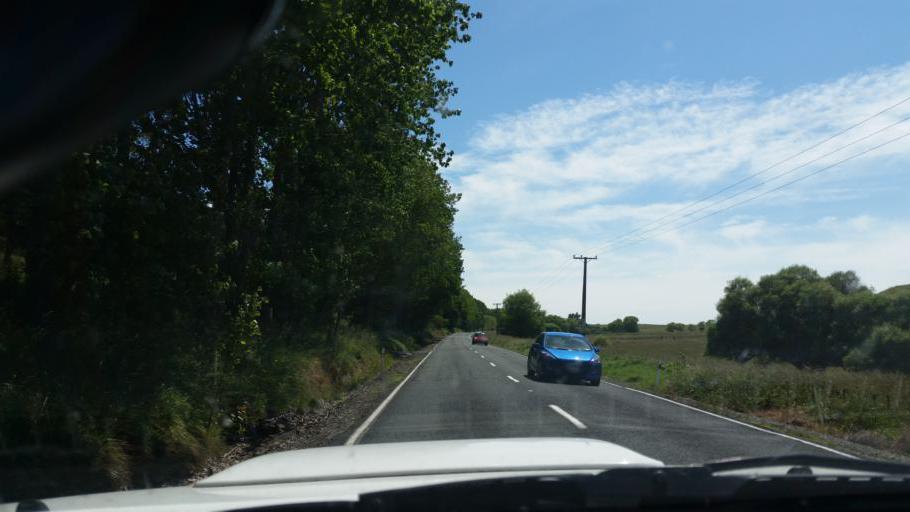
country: NZ
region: Auckland
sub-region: Auckland
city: Wellsford
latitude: -36.1946
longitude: 174.3996
